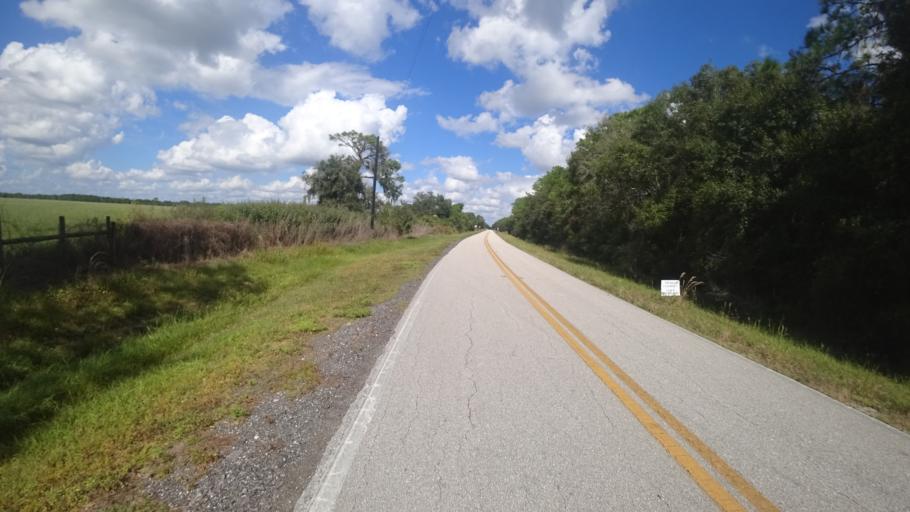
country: US
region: Florida
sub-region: Sarasota County
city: Warm Mineral Springs
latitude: 27.2591
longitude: -82.1217
